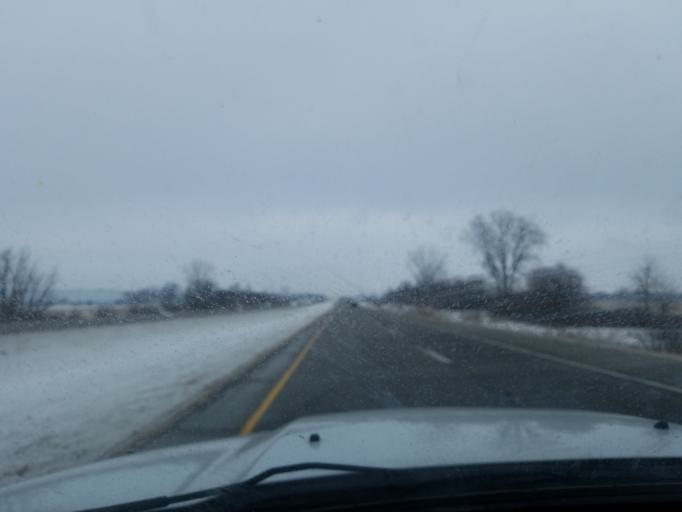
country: US
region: Indiana
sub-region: Marshall County
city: Argos
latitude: 41.2266
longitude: -86.2610
